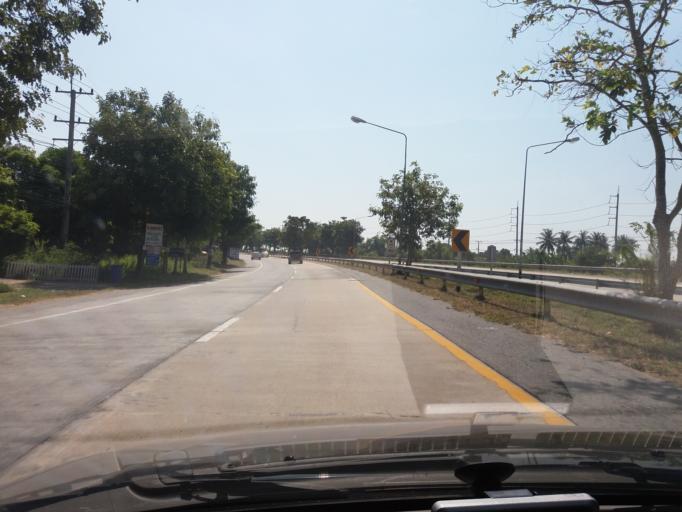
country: TH
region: Chai Nat
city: Chai Nat
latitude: 15.1484
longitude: 100.1405
